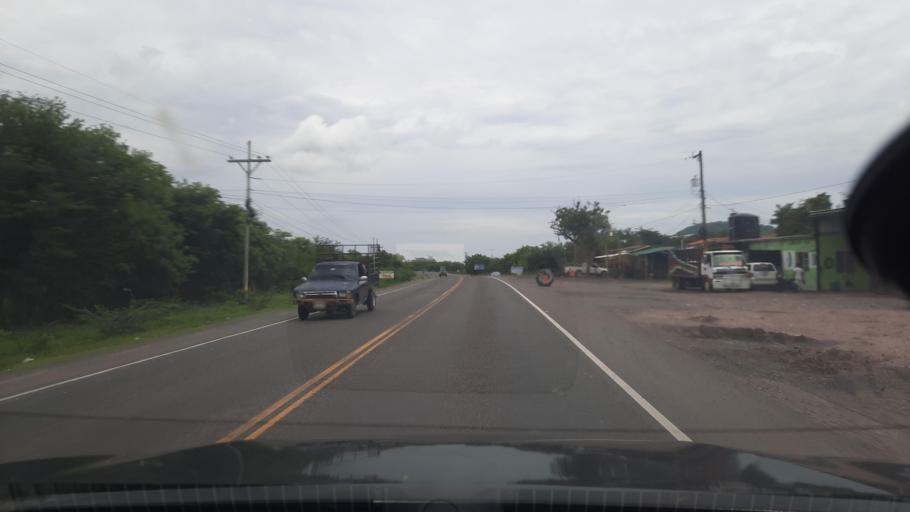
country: HN
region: Valle
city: Jicaro Galan
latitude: 13.5219
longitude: -87.4390
